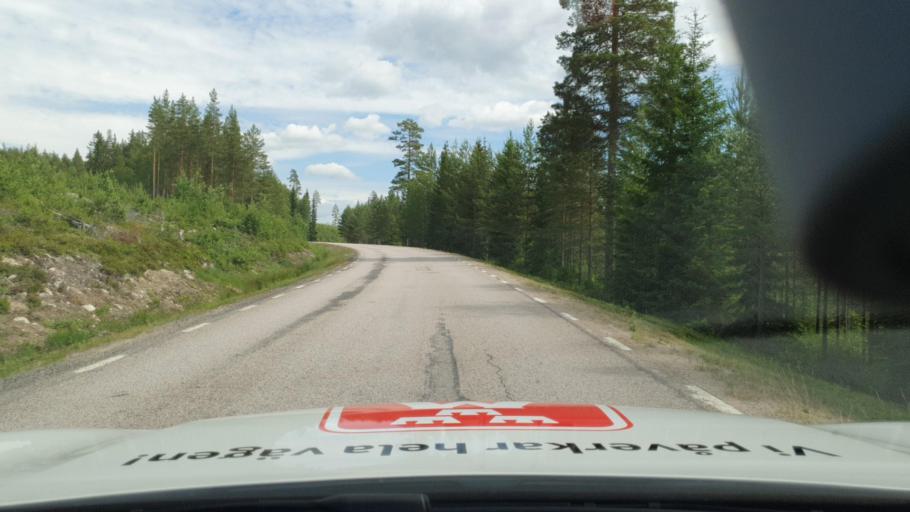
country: NO
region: Hedmark
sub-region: Asnes
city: Flisa
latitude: 60.6960
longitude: 12.5402
